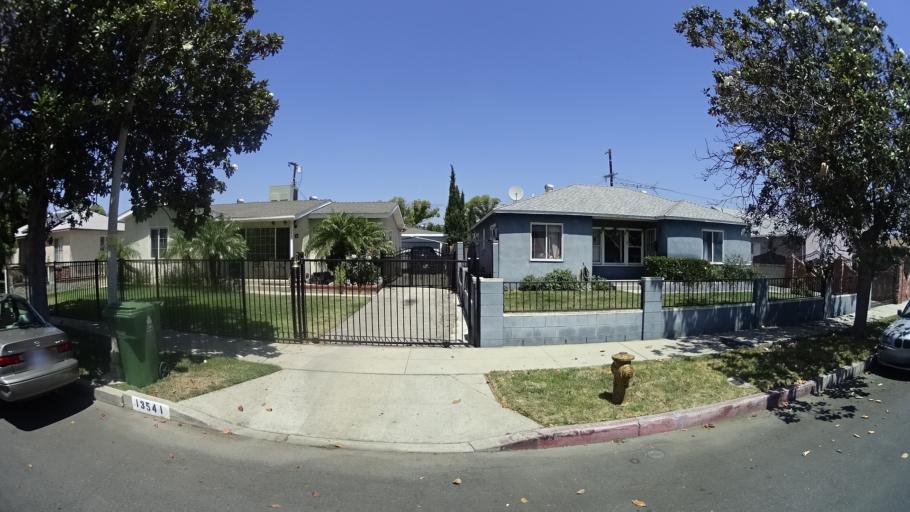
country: US
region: California
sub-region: Los Angeles County
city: San Fernando
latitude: 34.2360
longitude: -118.4272
